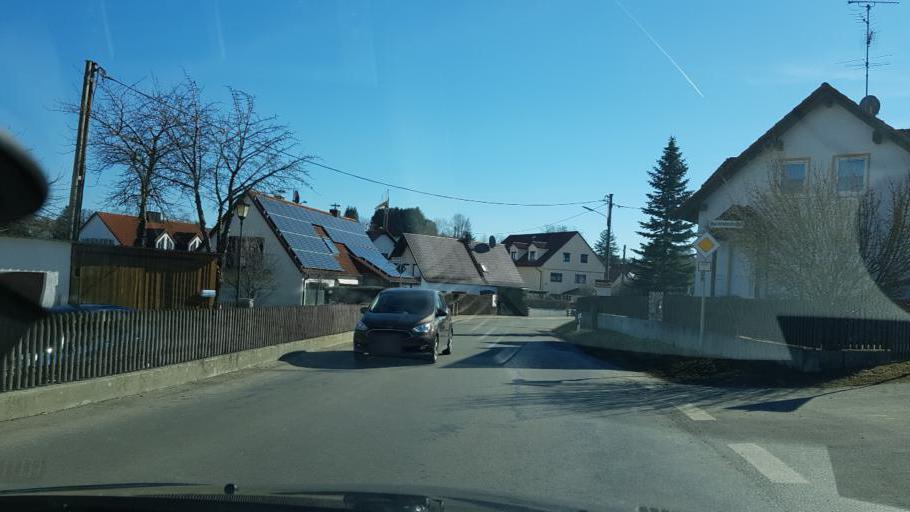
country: DE
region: Bavaria
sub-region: Upper Bavaria
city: Oberschweinbach
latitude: 48.2390
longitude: 11.1546
